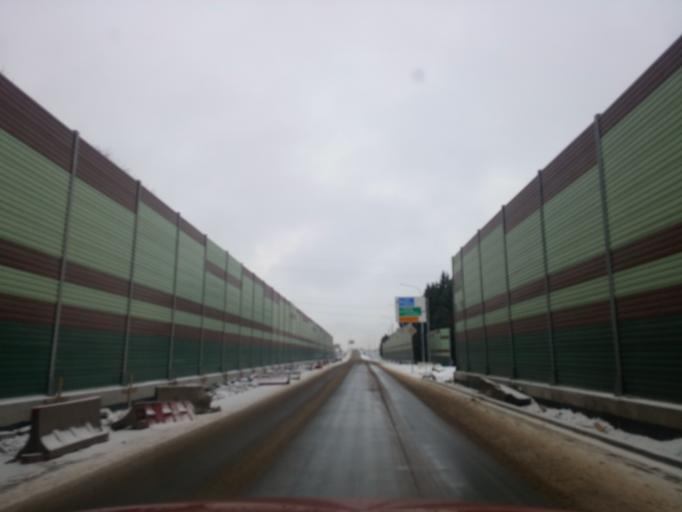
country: RU
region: Tverskaya
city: Likhoslavl'
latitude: 56.9854
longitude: 35.4405
